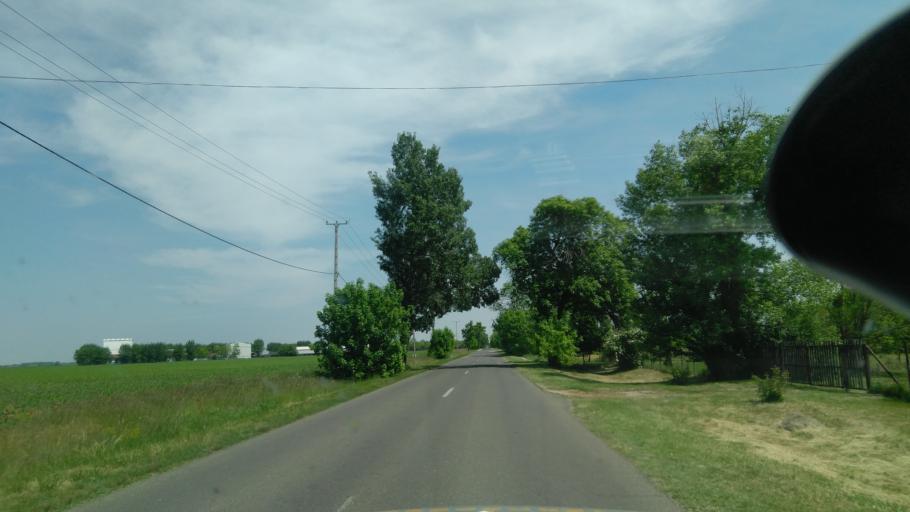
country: HU
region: Csongrad
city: Szekkutas
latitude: 46.5709
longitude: 20.5573
